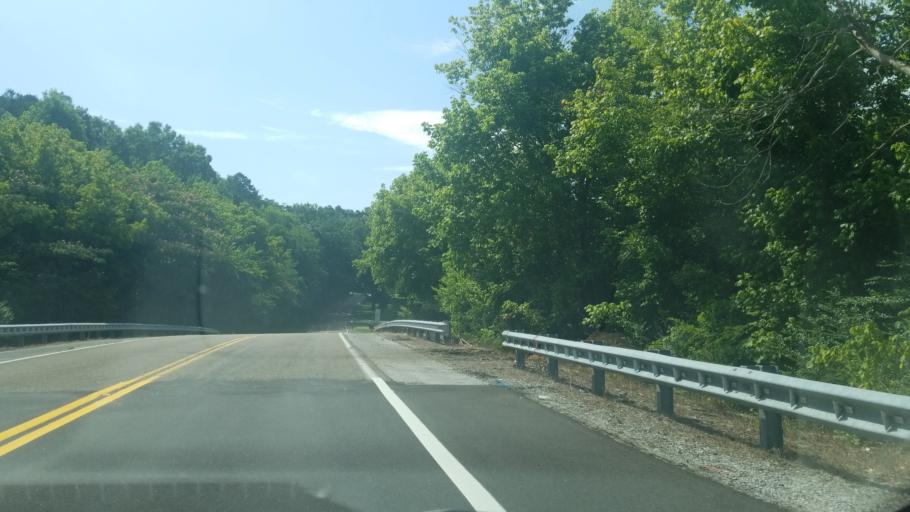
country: US
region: Tennessee
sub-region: Hamilton County
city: Lakesite
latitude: 35.1802
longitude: -85.0672
